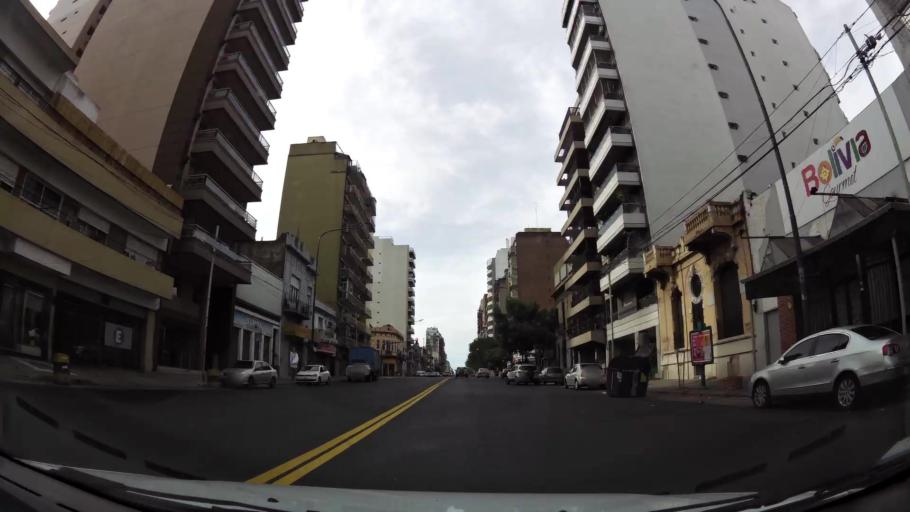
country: AR
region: Buenos Aires F.D.
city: Villa Santa Rita
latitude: -34.6340
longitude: -58.4681
